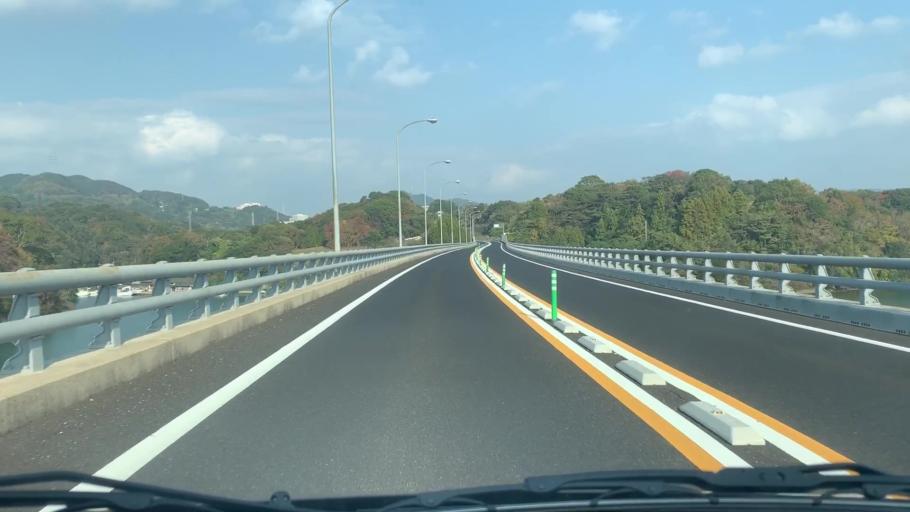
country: JP
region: Nagasaki
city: Sasebo
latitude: 33.0774
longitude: 129.7704
